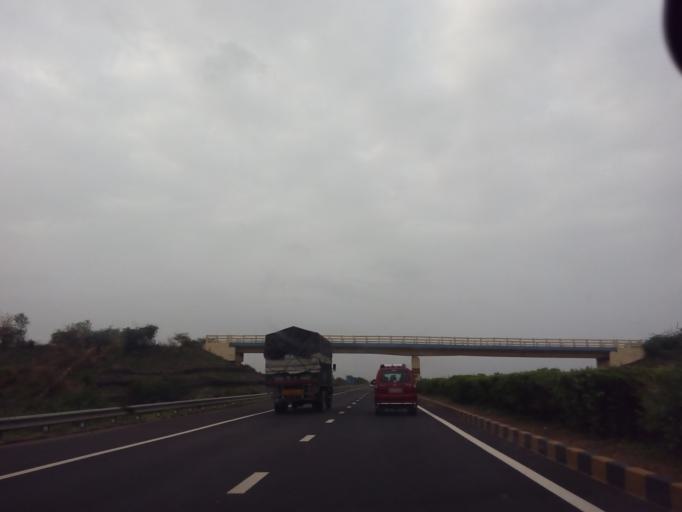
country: IN
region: Gujarat
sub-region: Kheda
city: Nadiad
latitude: 22.7823
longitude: 72.8460
